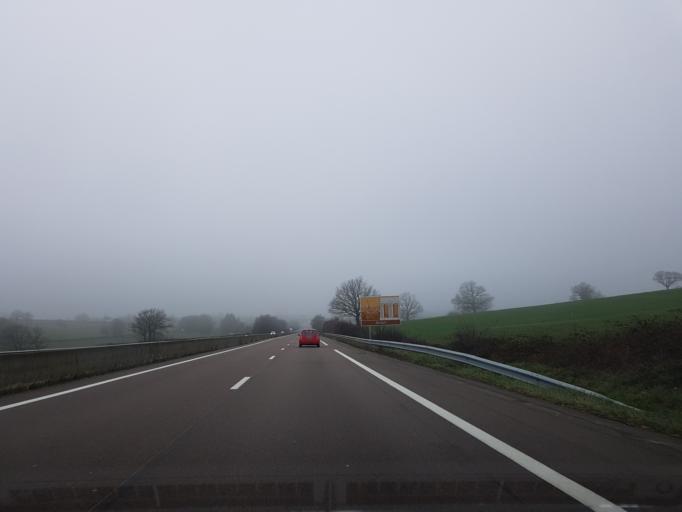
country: FR
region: Bourgogne
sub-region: Departement de Saone-et-Loire
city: Ecuisses
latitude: 46.7452
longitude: 4.5259
